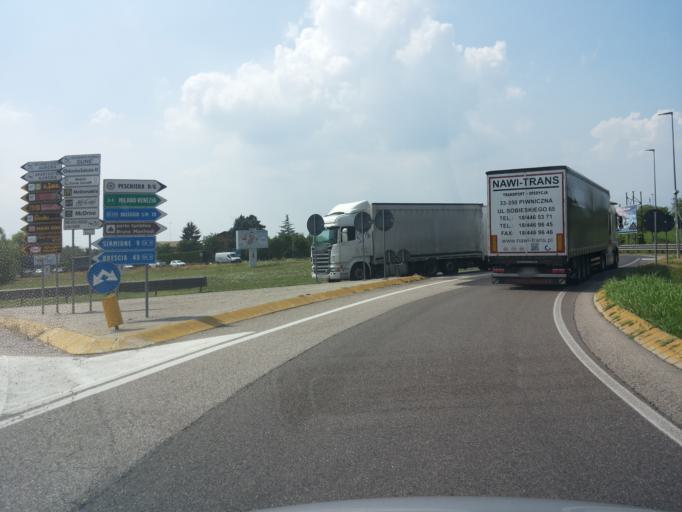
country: IT
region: Veneto
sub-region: Provincia di Verona
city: Cavalcaselle
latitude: 45.4324
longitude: 10.7062
